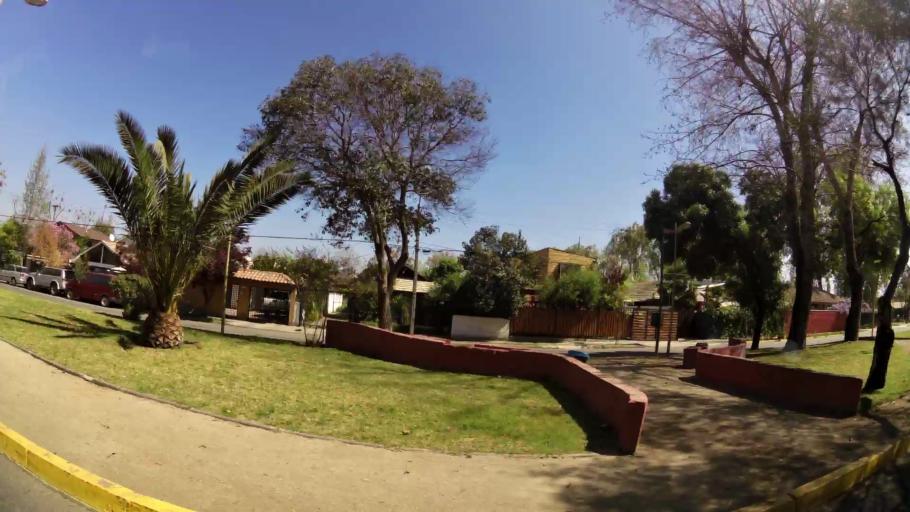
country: CL
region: Santiago Metropolitan
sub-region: Provincia de Santiago
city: Villa Presidente Frei, Nunoa, Santiago, Chile
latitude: -33.4179
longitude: -70.5464
